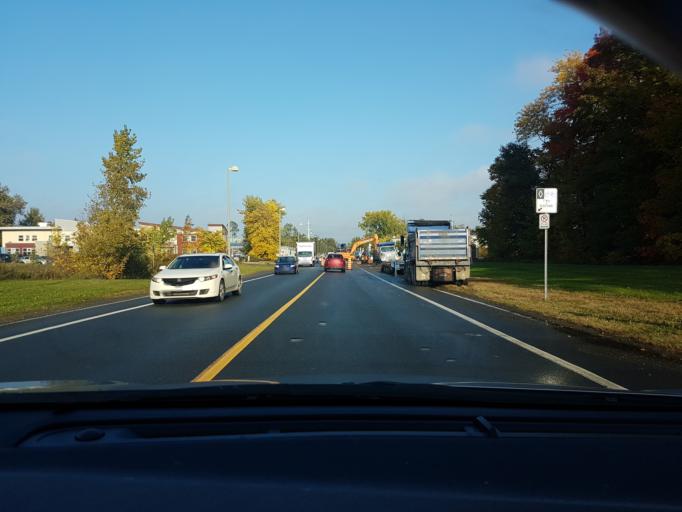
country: CA
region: Quebec
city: L'Ancienne-Lorette
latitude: 46.7971
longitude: -71.3039
